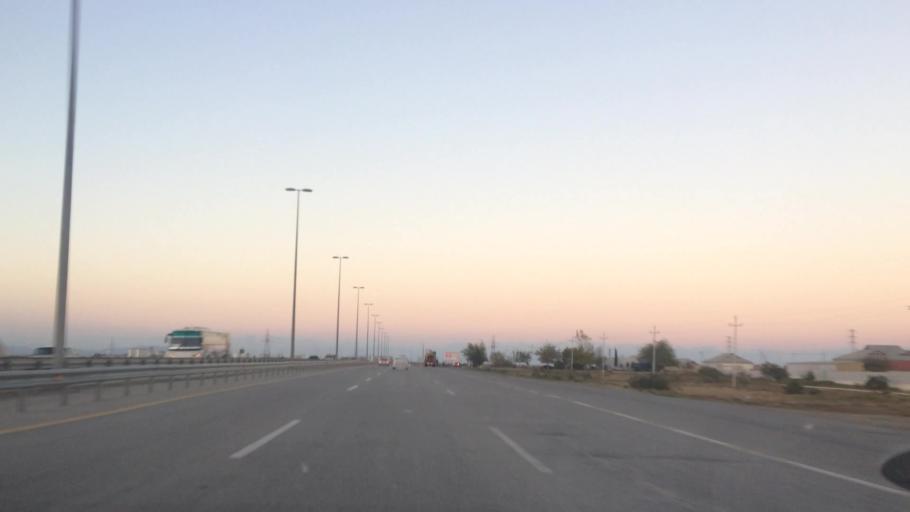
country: AZ
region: Baki
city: Qobustan
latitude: 39.9861
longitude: 49.4267
